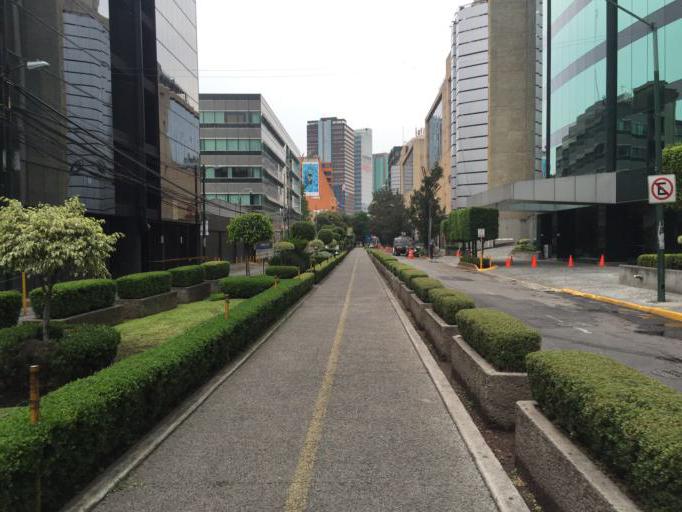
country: MX
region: Mexico City
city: Miguel Hidalgo
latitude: 19.4290
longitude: -99.2057
